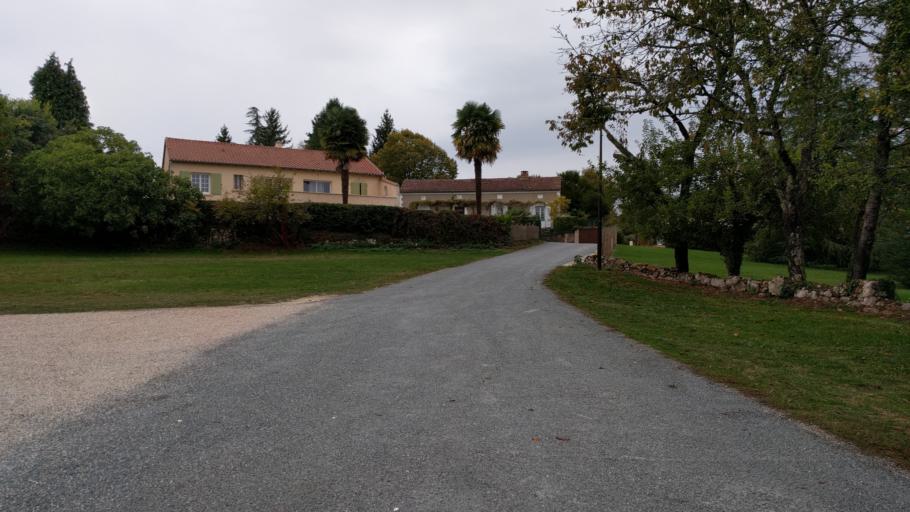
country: FR
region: Aquitaine
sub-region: Departement de la Dordogne
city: Mouleydier
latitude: 44.8967
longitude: 0.6444
